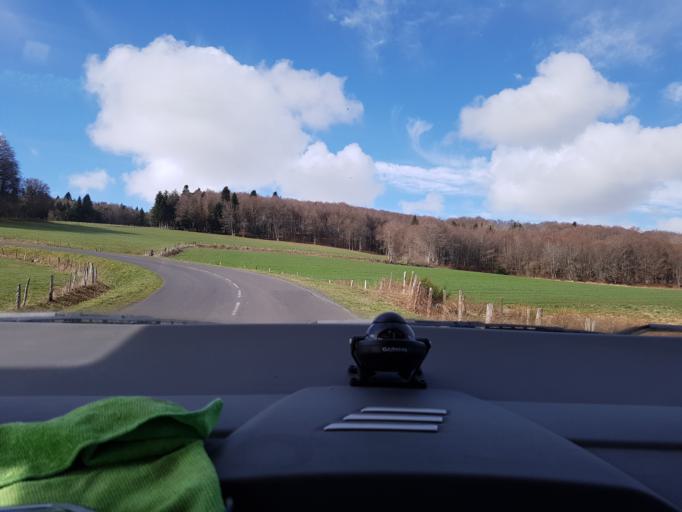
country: FR
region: Auvergne
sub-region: Departement du Cantal
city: Saint-Flour
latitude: 45.1201
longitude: 3.1487
